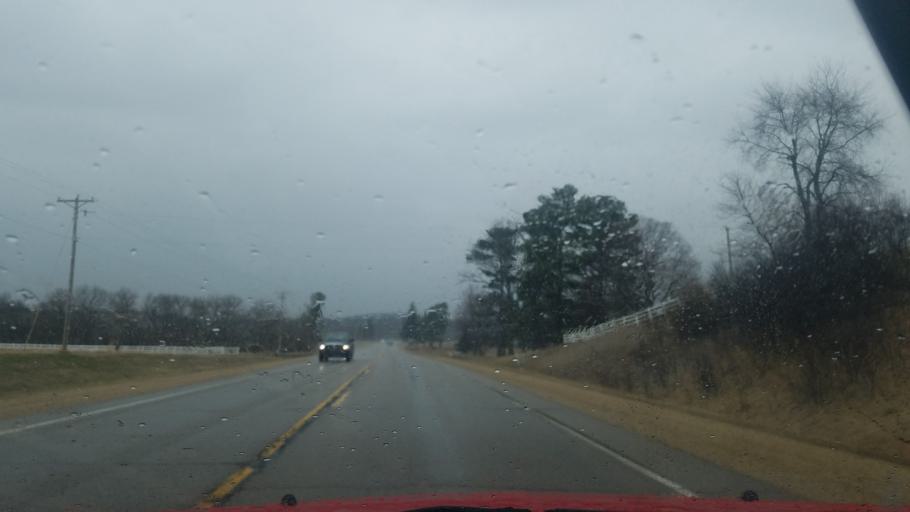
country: US
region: Wisconsin
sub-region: Dunn County
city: Menomonie
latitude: 44.9270
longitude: -91.9251
